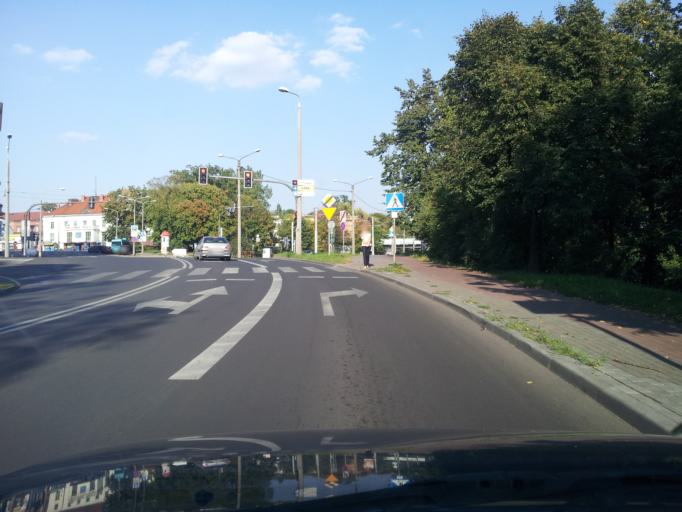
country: PL
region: Kujawsko-Pomorskie
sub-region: Torun
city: Torun
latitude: 53.0105
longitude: 18.6179
